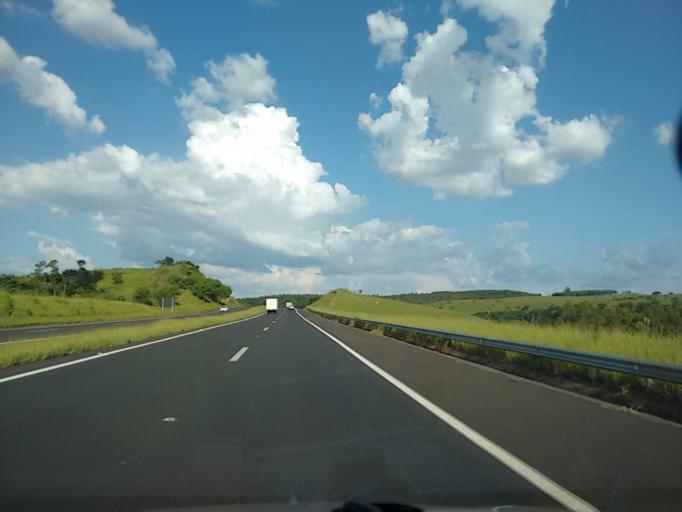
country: BR
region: Sao Paulo
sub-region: Duartina
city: Duartina
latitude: -22.3193
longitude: -49.4855
